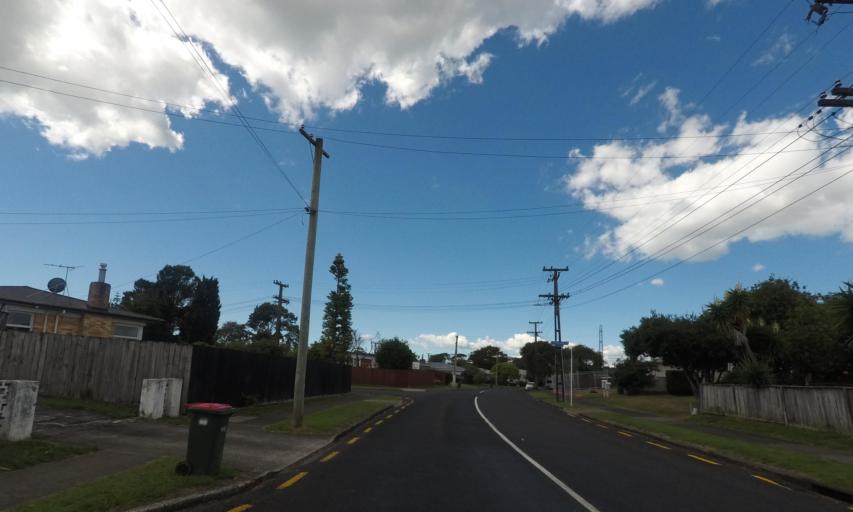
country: NZ
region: Auckland
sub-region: Auckland
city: Tamaki
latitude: -36.9189
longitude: 174.8653
